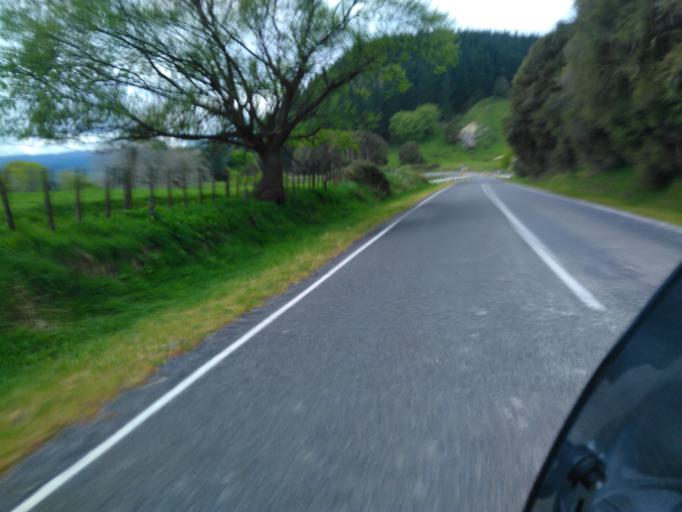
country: NZ
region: Hawke's Bay
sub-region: Wairoa District
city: Wairoa
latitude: -38.8999
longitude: 177.4736
